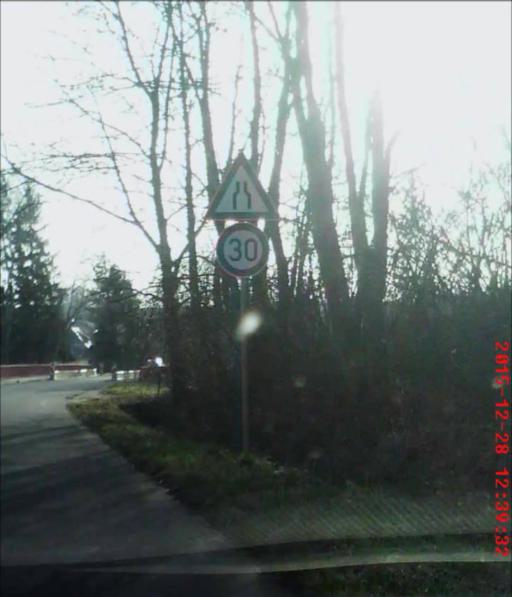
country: DE
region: Thuringia
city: Ossmanstedt
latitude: 51.0143
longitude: 11.4238
